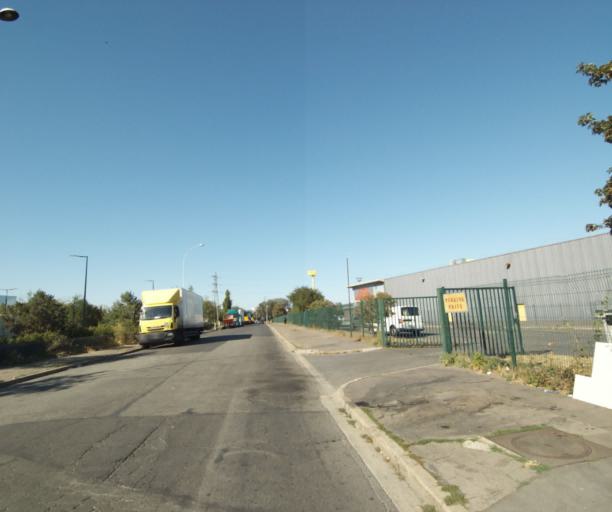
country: FR
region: Ile-de-France
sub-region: Departement des Hauts-de-Seine
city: Villeneuve-la-Garenne
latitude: 48.9286
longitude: 2.3196
